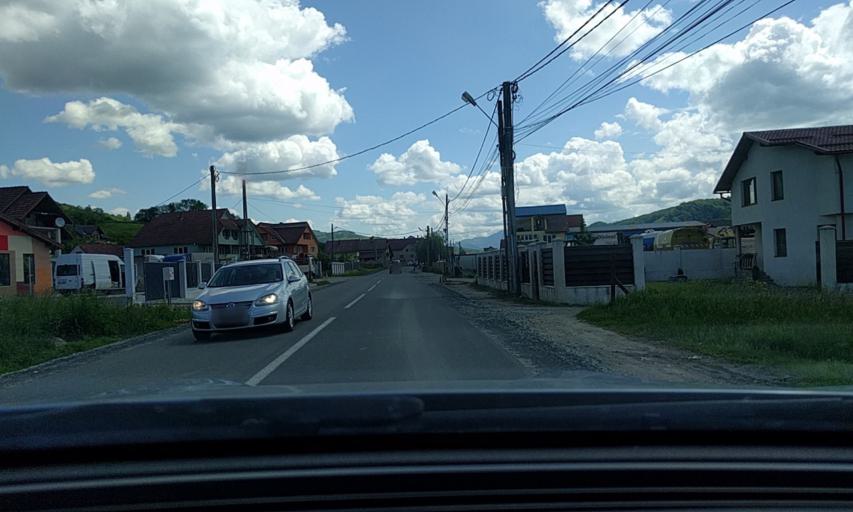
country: RO
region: Bistrita-Nasaud
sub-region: Comuna Rebrisoara
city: Rebrisoara
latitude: 47.2851
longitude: 24.4292
